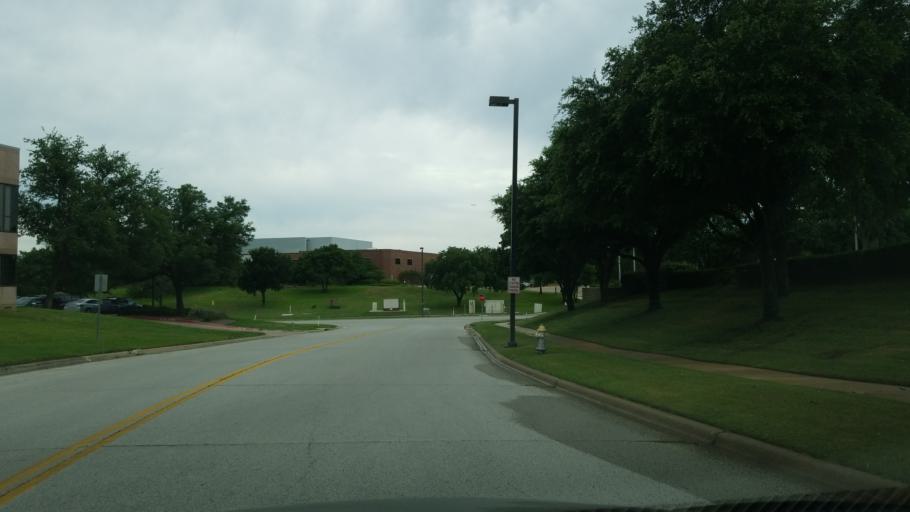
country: US
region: Texas
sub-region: Dallas County
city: Coppell
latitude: 32.8941
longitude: -96.9845
